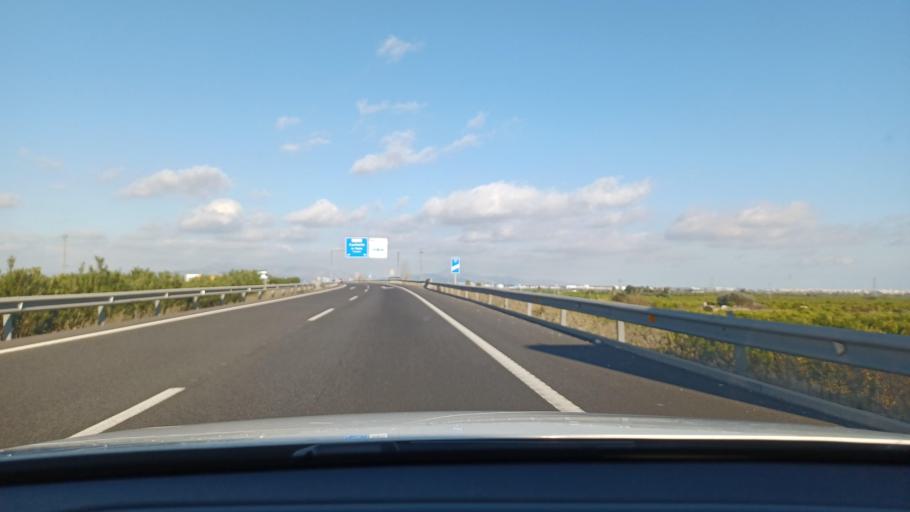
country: ES
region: Valencia
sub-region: Provincia de Castello
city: Betxi
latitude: 39.9227
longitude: -0.1937
